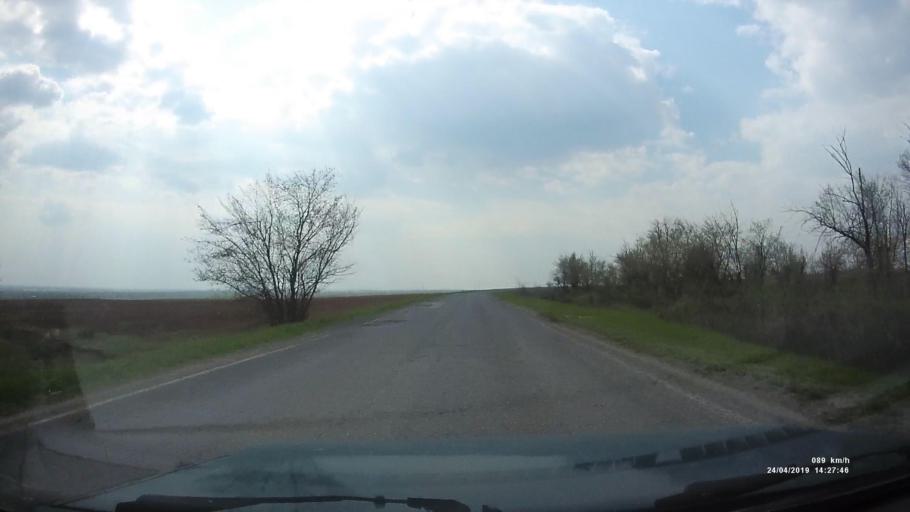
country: RU
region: Kalmykiya
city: Arshan'
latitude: 46.3337
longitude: 44.0365
